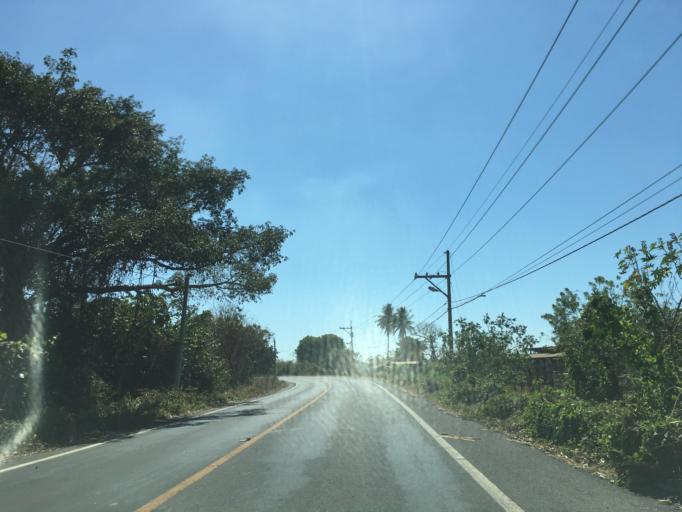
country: GT
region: Escuintla
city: Puerto San Jose
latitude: 13.9803
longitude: -90.8877
